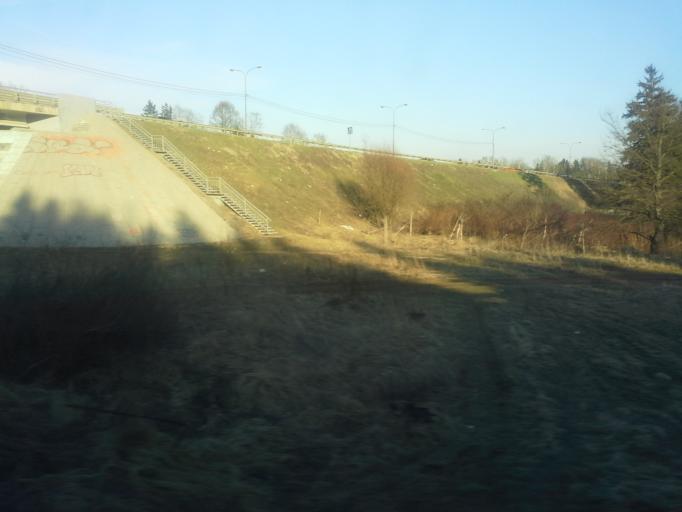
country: RU
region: Moskovskaya
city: Yermolino
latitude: 56.1245
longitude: 37.5184
